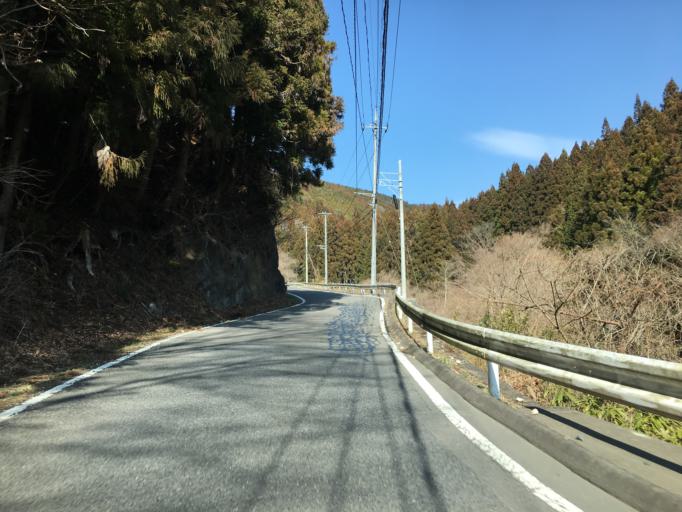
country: JP
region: Ibaraki
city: Daigo
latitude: 36.8066
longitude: 140.4986
